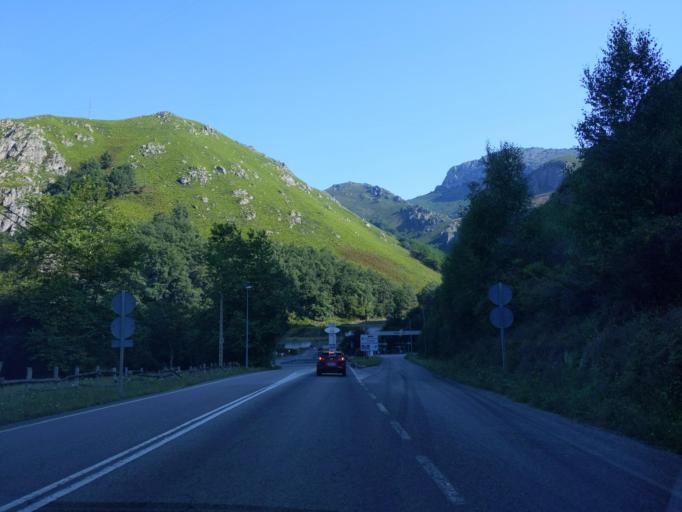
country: ES
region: Asturias
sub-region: Province of Asturias
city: Pola de Laviana
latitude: 43.2313
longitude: -5.4741
